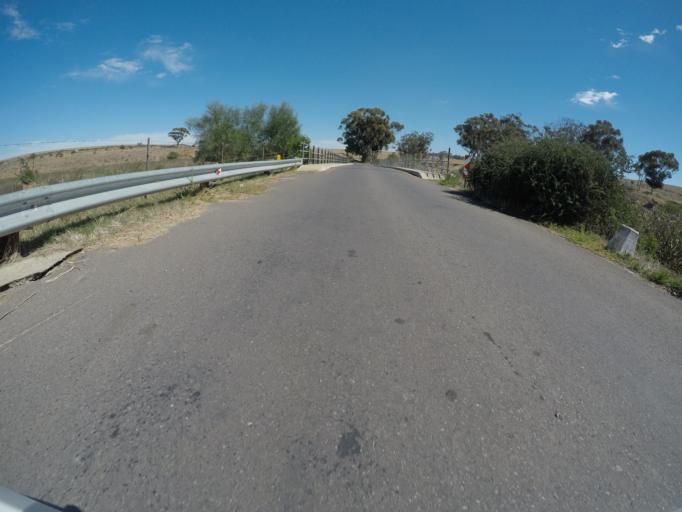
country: ZA
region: Western Cape
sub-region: City of Cape Town
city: Atlantis
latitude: -33.6770
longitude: 18.6062
